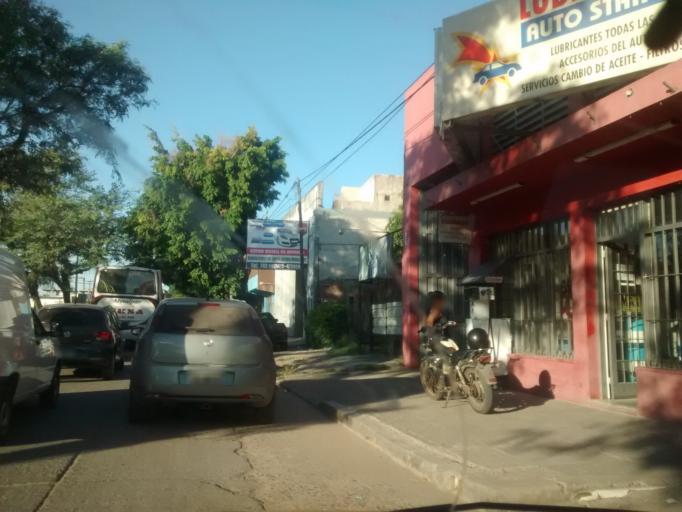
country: AR
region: Chaco
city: Resistencia
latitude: -27.4561
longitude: -59.0060
